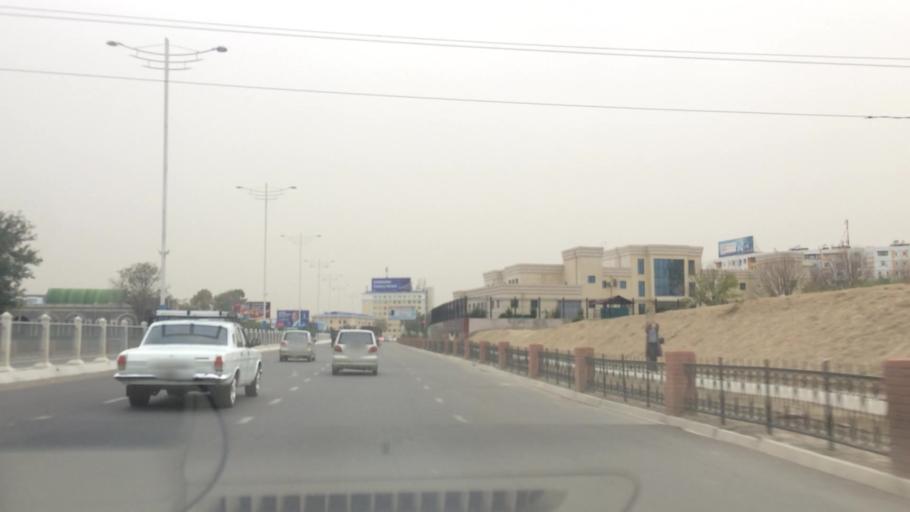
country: UZ
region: Toshkent Shahri
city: Bektemir
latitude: 41.3046
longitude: 69.3104
